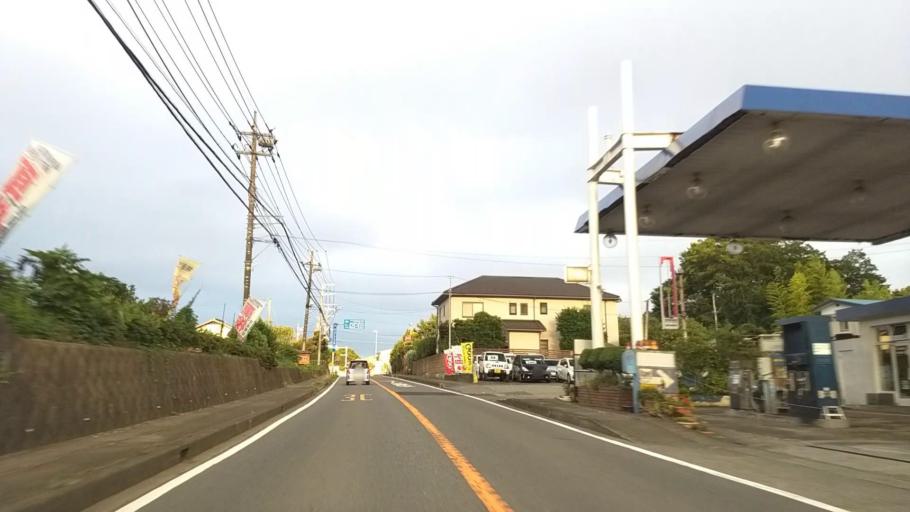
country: JP
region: Kanagawa
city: Atsugi
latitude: 35.4716
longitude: 139.3119
